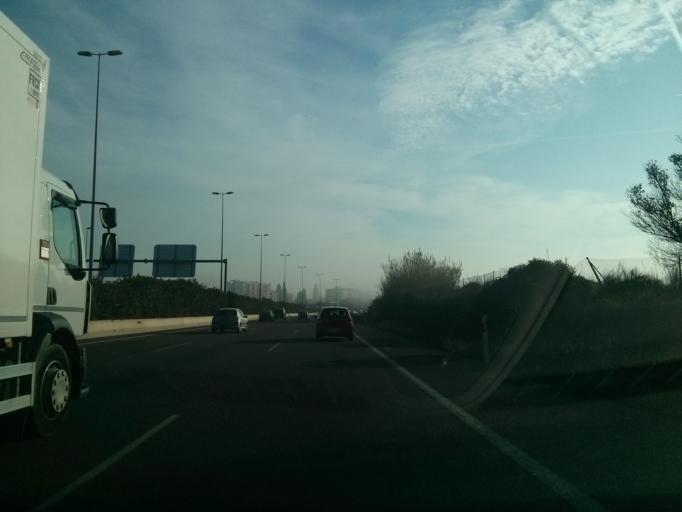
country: ES
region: Valencia
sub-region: Provincia de Valencia
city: Paterna
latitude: 39.4941
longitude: -0.4252
